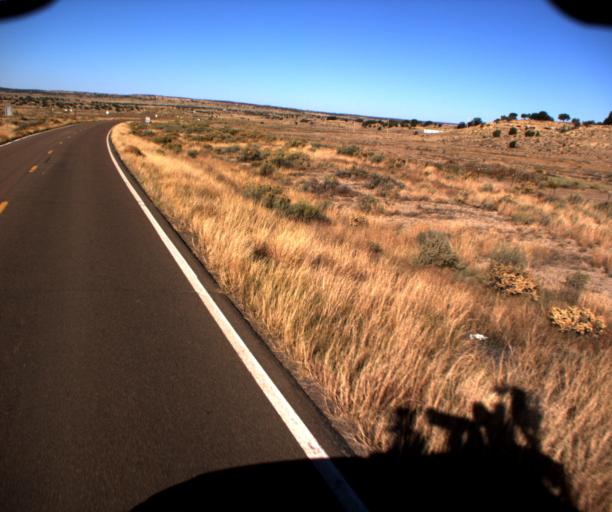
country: US
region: Arizona
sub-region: Apache County
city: Ganado
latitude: 35.7465
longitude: -109.8630
